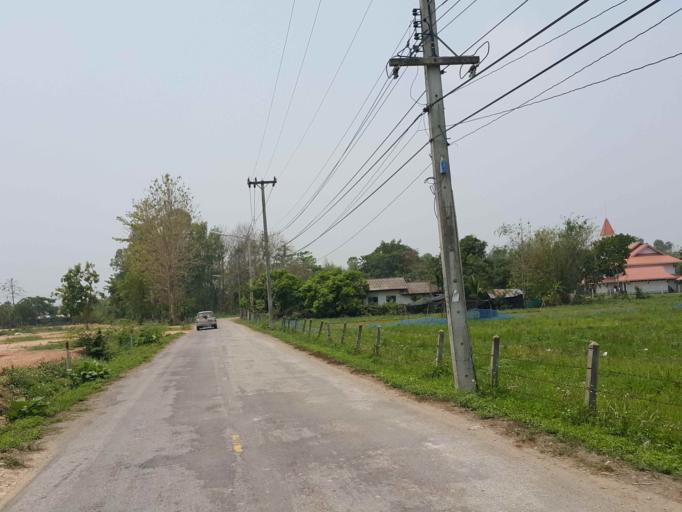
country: TH
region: Chiang Mai
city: San Sai
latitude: 18.8950
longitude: 99.0769
